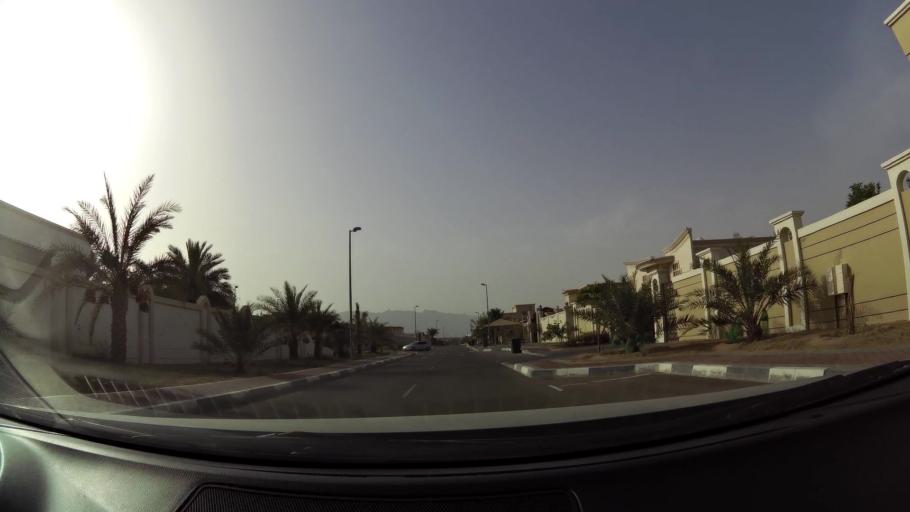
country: AE
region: Abu Dhabi
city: Al Ain
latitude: 24.1233
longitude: 55.6942
